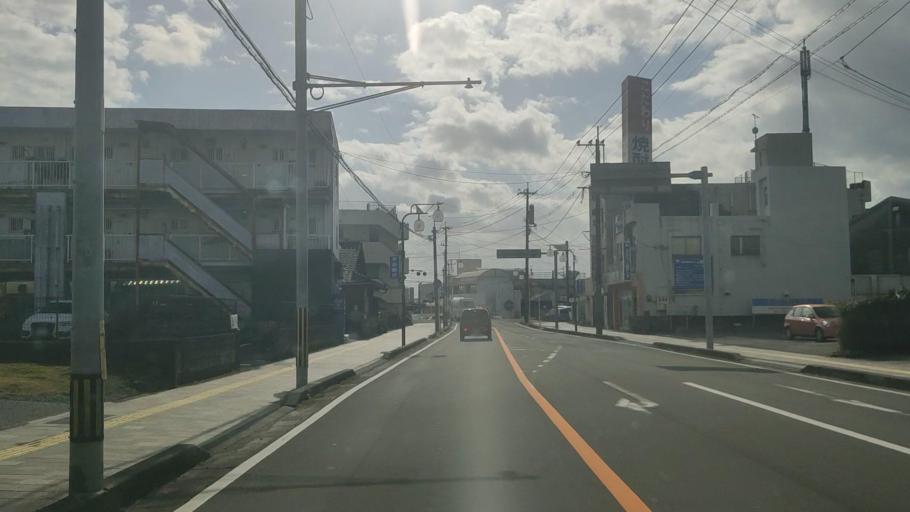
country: JP
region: Kagoshima
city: Kajiki
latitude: 31.7406
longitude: 130.6678
